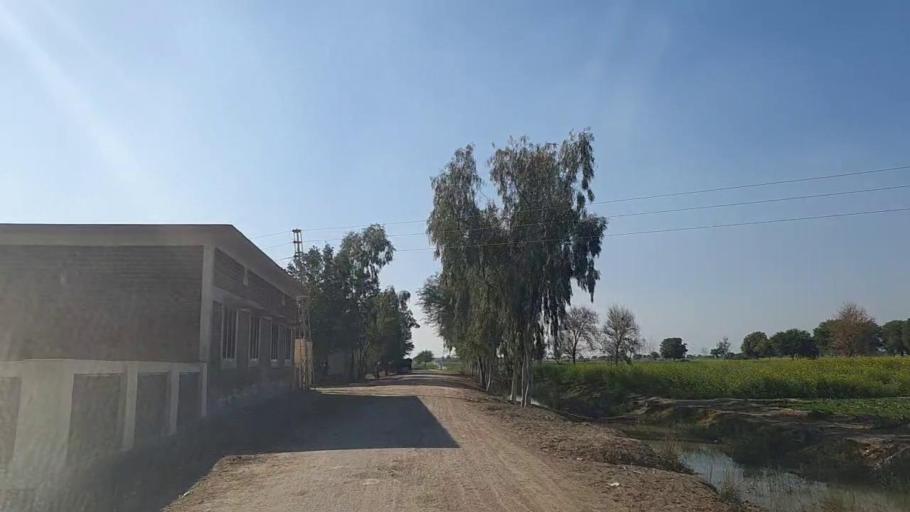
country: PK
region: Sindh
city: Shahpur Chakar
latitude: 26.2176
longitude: 68.5955
